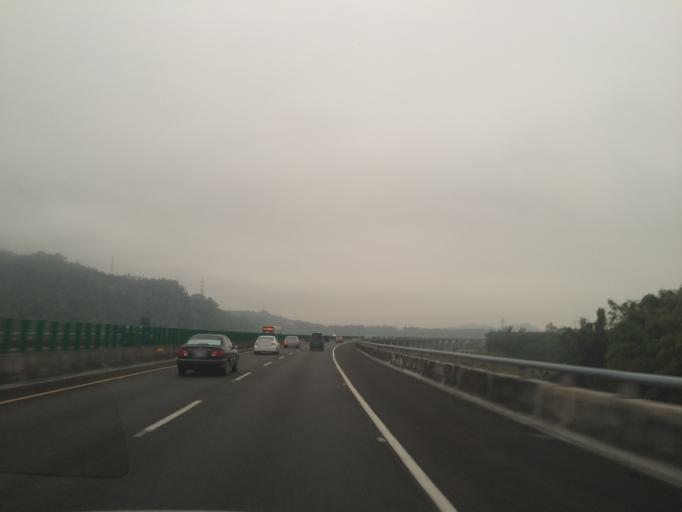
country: TW
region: Taiwan
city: Zhongxing New Village
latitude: 23.9822
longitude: 120.7702
